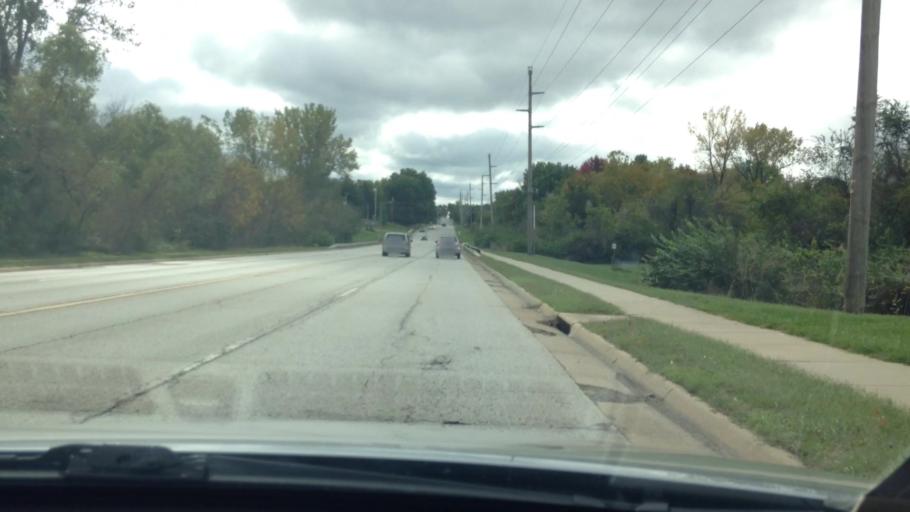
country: US
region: Kansas
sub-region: Leavenworth County
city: Leavenworth
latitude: 39.2819
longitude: -94.9279
